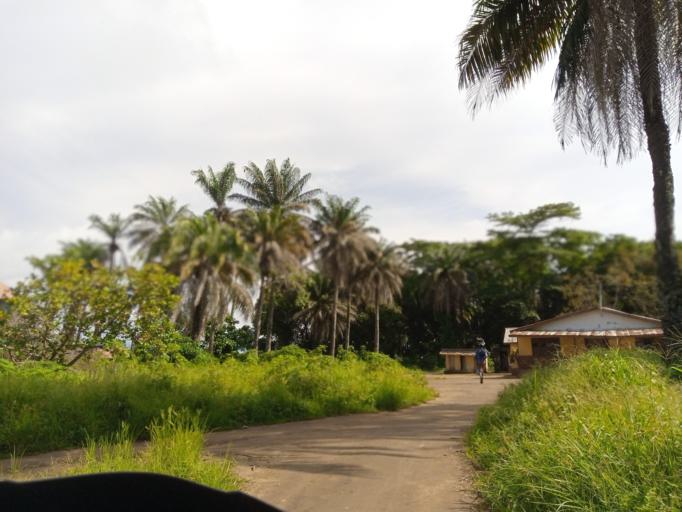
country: SL
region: Northern Province
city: Masoyila
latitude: 8.6092
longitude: -13.2041
